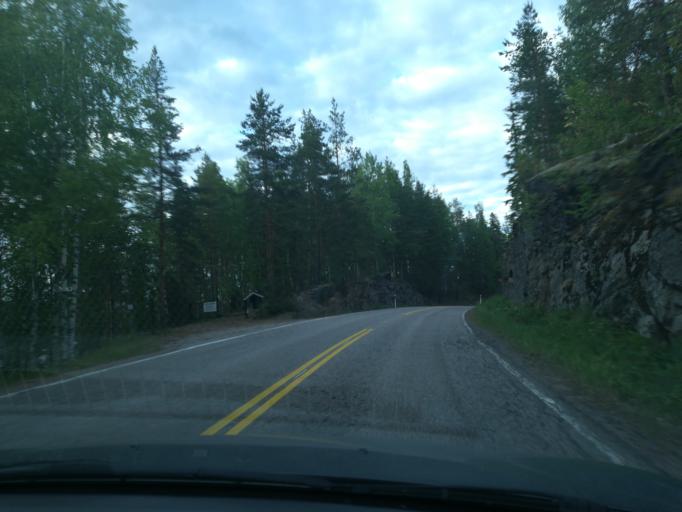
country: FI
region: Southern Savonia
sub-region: Mikkeli
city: Puumala
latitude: 61.5611
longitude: 27.9760
